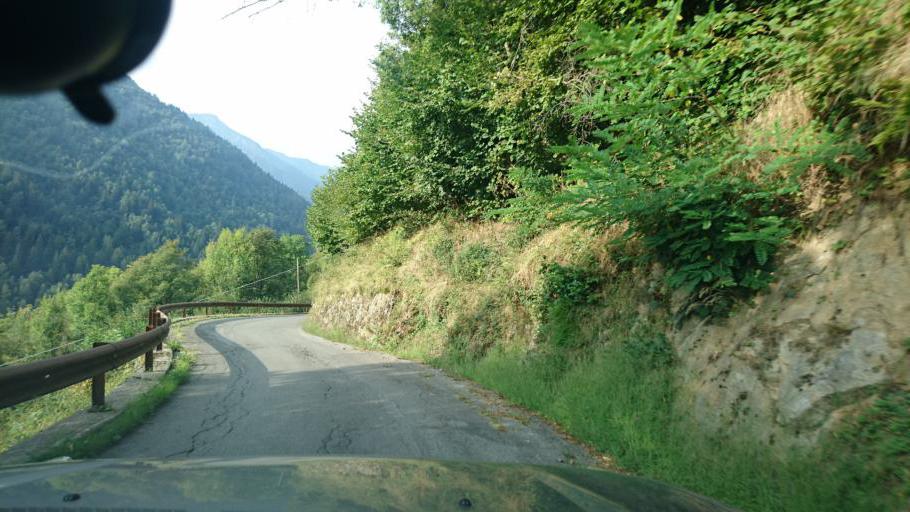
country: IT
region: Lombardy
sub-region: Provincia di Brescia
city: Paisco Loveno
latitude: 46.0671
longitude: 10.2611
